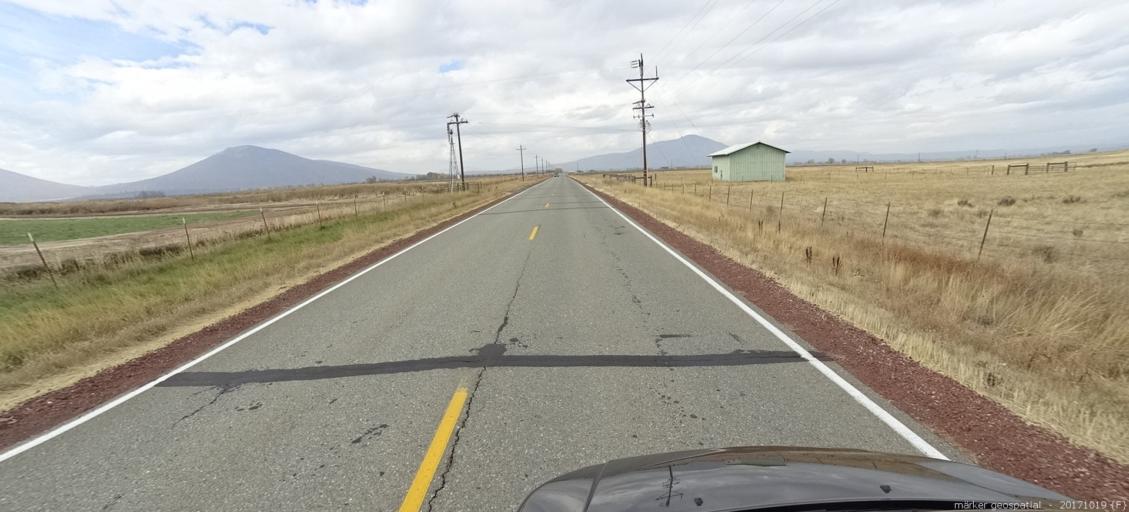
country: US
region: California
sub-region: Shasta County
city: Burney
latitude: 41.0509
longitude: -121.4265
